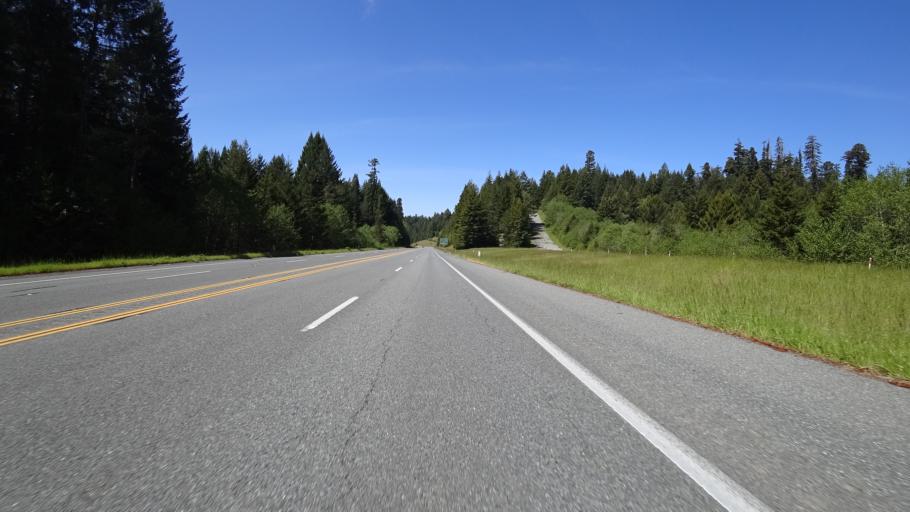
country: US
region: California
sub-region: Humboldt County
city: Westhaven-Moonstone
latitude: 41.3596
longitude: -124.0046
